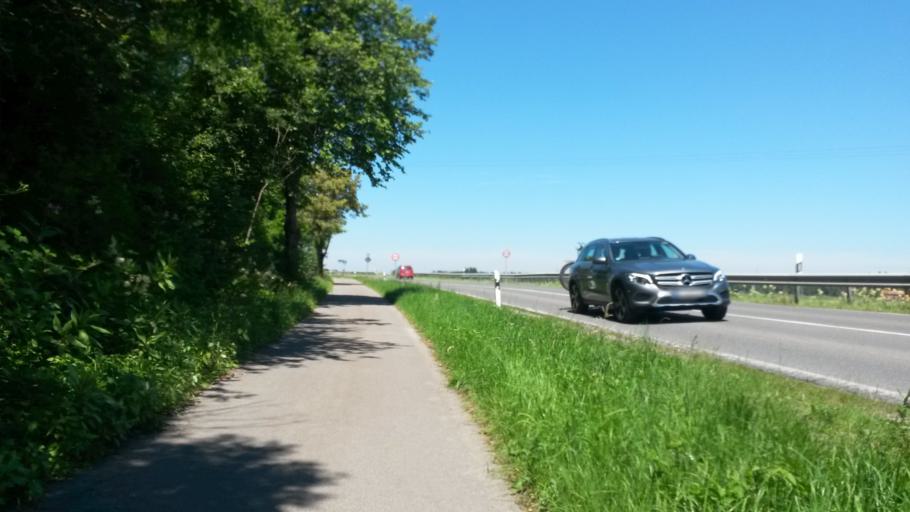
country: DE
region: Bavaria
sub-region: Upper Bavaria
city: Grassau
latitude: 47.7879
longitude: 12.4235
